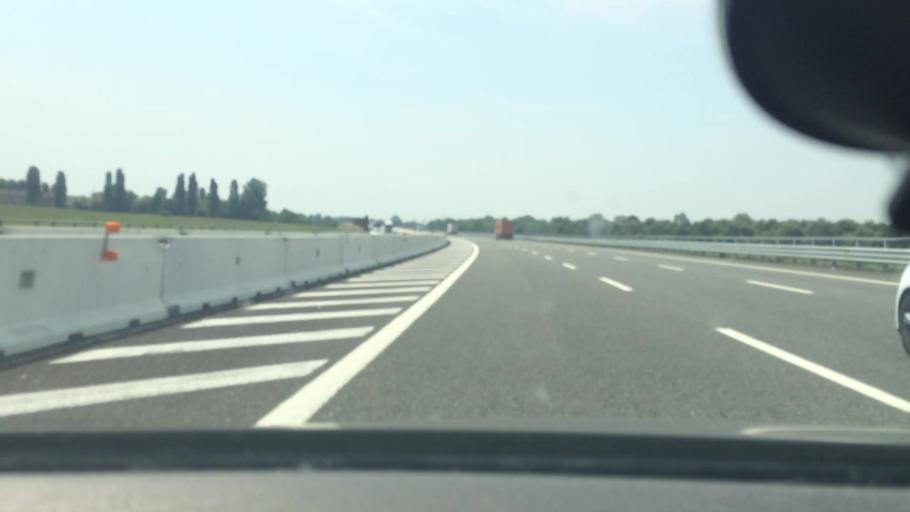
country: IT
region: Lombardy
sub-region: Provincia di Lodi
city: Cassino d'Alberi
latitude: 45.3865
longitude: 9.3754
